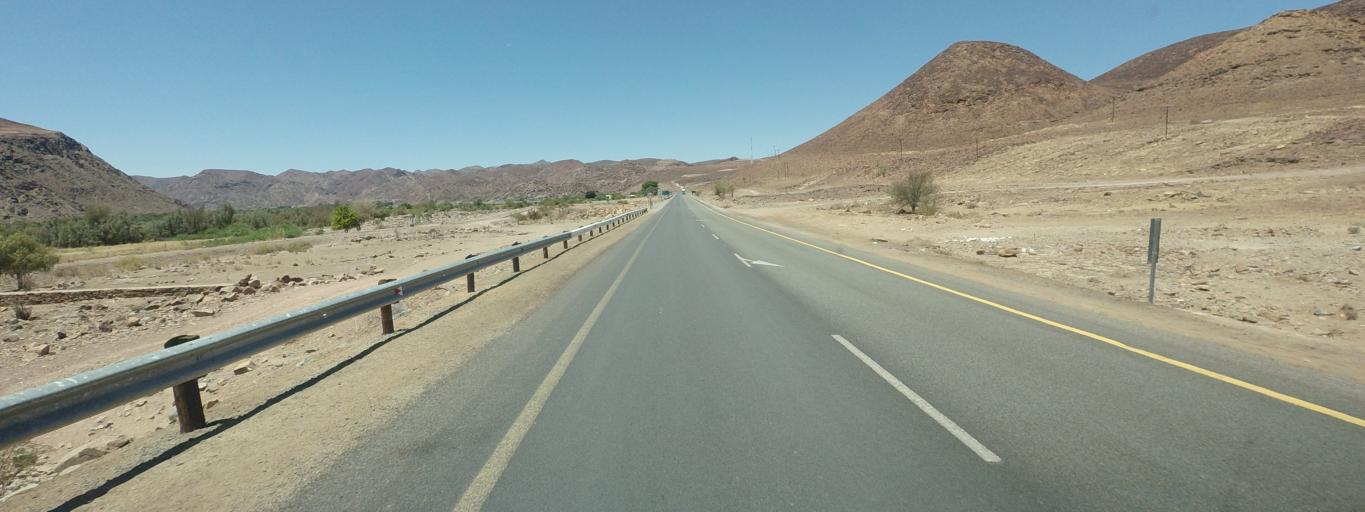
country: ZA
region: Northern Cape
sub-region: Namakwa District Municipality
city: Port Nolloth
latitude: -28.7755
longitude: 17.6367
